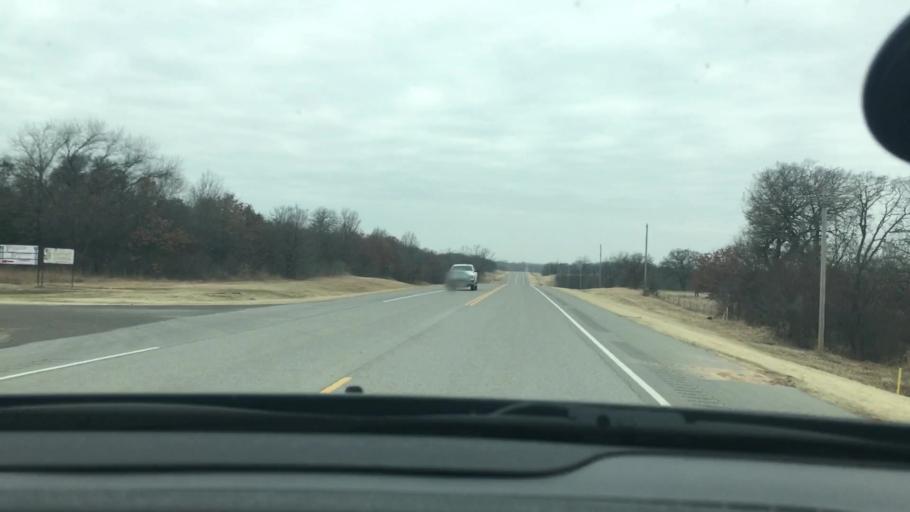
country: US
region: Oklahoma
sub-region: Carter County
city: Healdton
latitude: 34.4924
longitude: -97.4265
